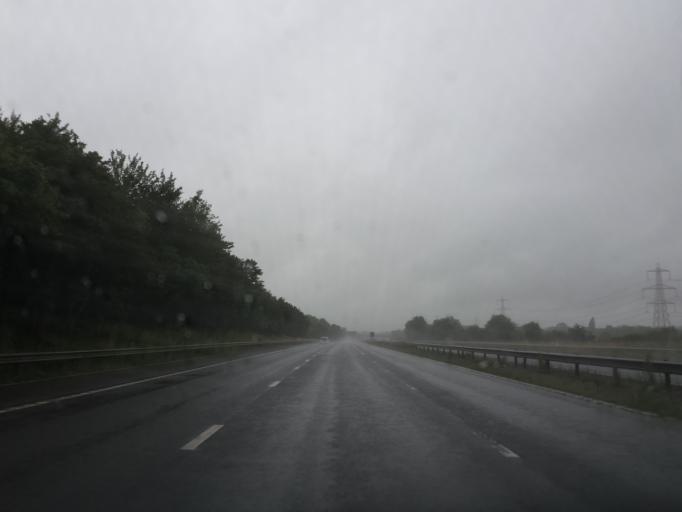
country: GB
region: England
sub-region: Leicestershire
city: Sapcote
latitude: 52.5317
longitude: -1.3248
